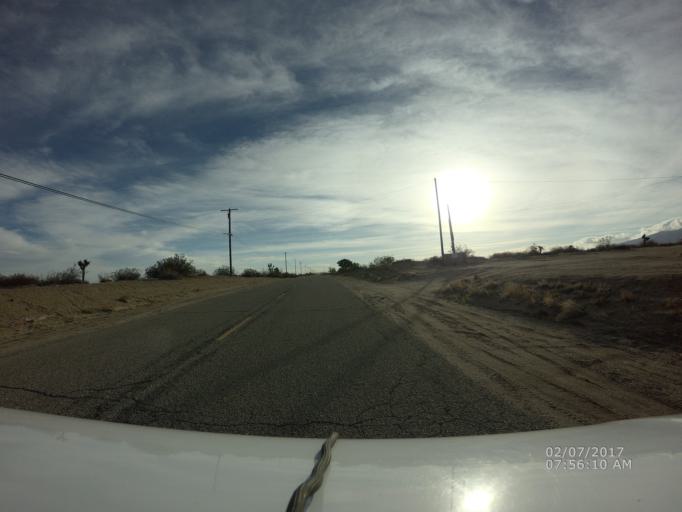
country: US
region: California
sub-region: Los Angeles County
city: Lake Los Angeles
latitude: 34.5873
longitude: -117.8000
